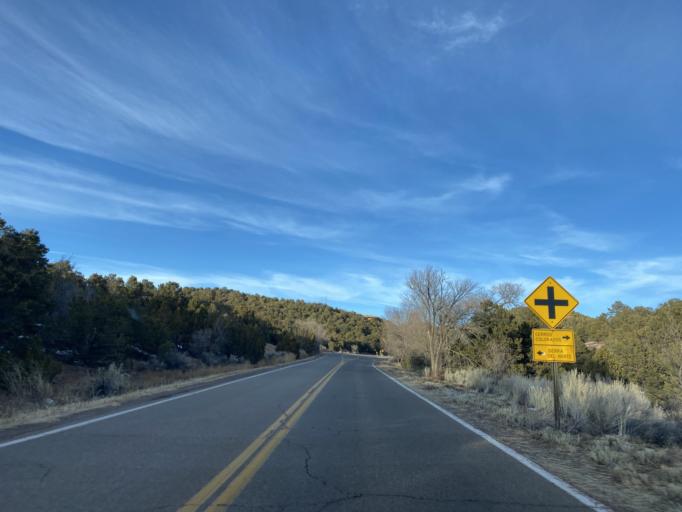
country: US
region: New Mexico
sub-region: Santa Fe County
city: Santa Fe
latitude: 35.7080
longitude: -105.8998
